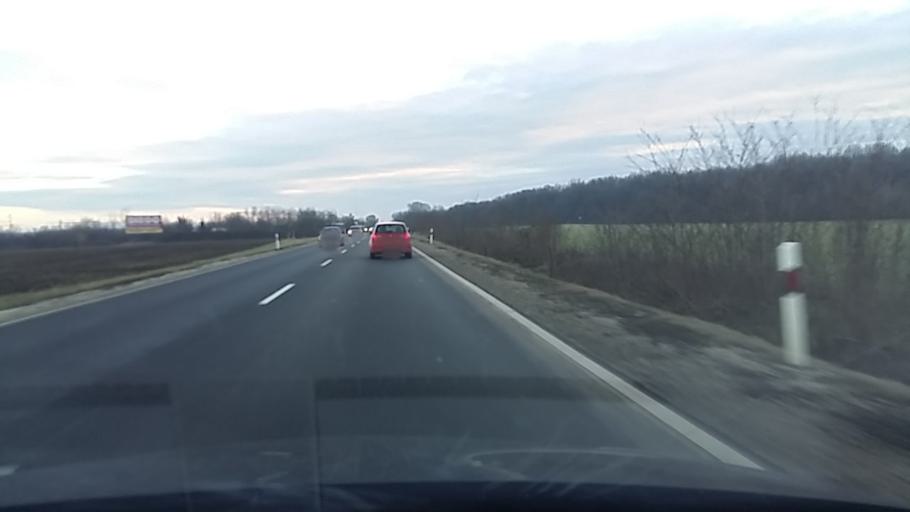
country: HU
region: Hajdu-Bihar
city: Debrecen
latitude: 47.5908
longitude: 21.6542
